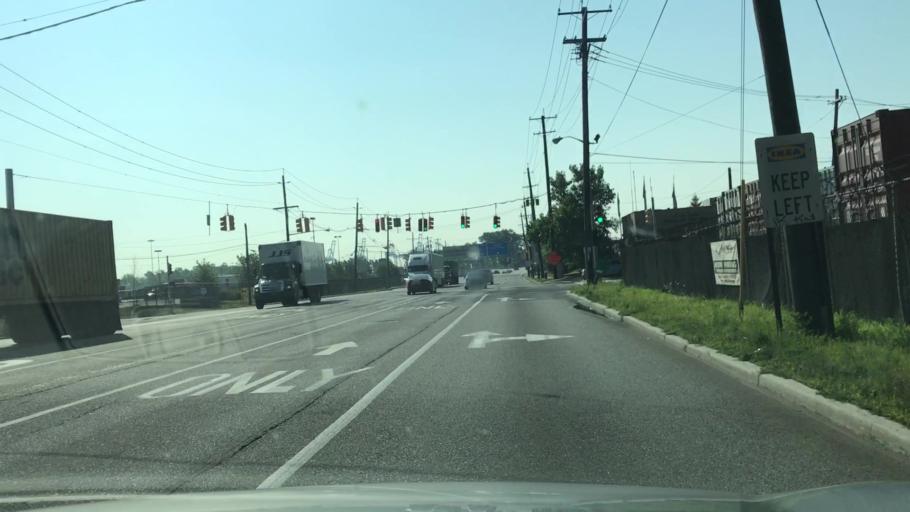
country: US
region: New Jersey
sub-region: Union County
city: Elizabeth
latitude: 40.6673
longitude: -74.1724
